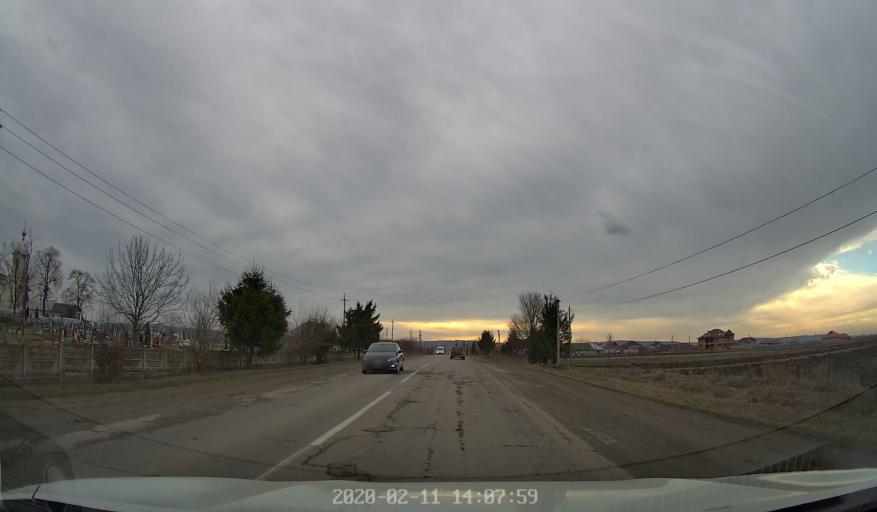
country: RO
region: Botosani
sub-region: Comuna Darabani
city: Bajura
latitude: 48.2418
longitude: 26.5484
